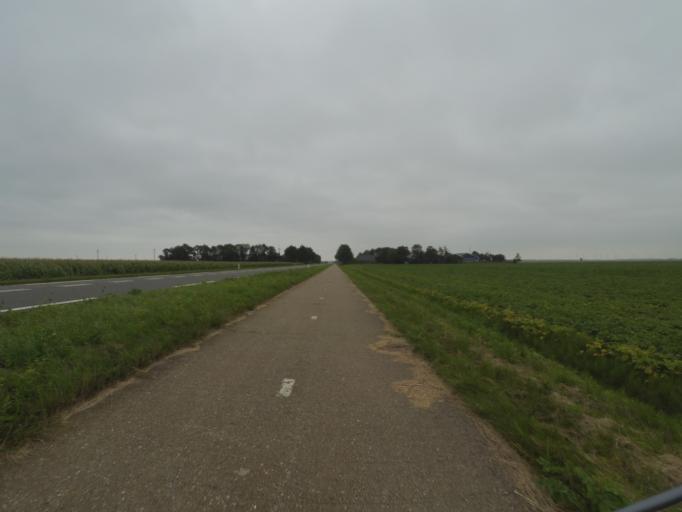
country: NL
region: Flevoland
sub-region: Gemeente Zeewolde
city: Zeewolde
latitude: 52.3798
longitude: 5.4504
